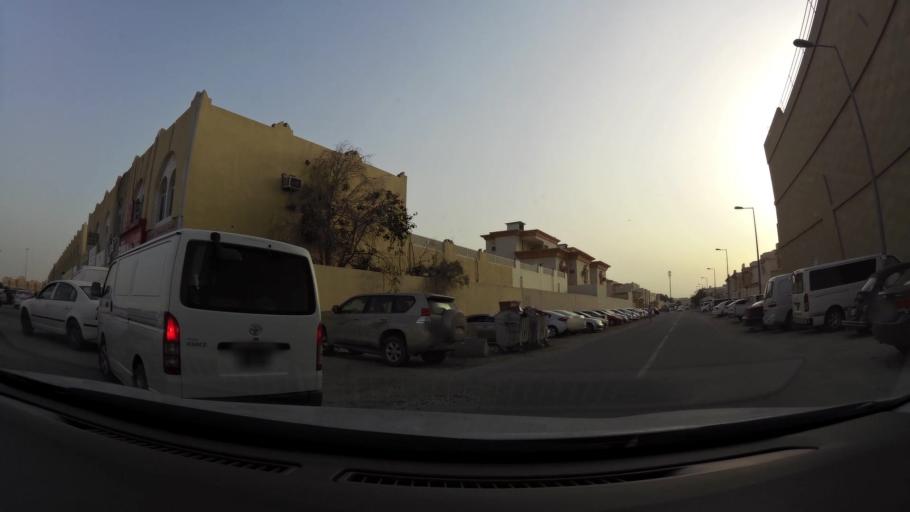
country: QA
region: Baladiyat ar Rayyan
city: Ar Rayyan
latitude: 25.2425
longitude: 51.4550
